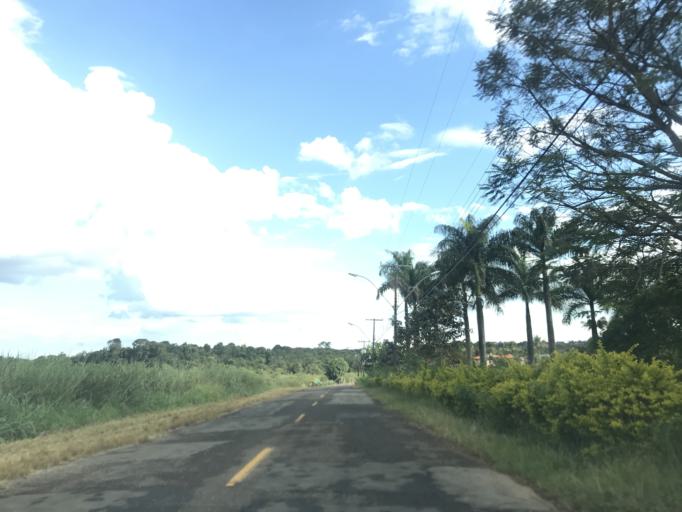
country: BR
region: Federal District
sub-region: Brasilia
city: Brasilia
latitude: -15.9159
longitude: -47.9423
